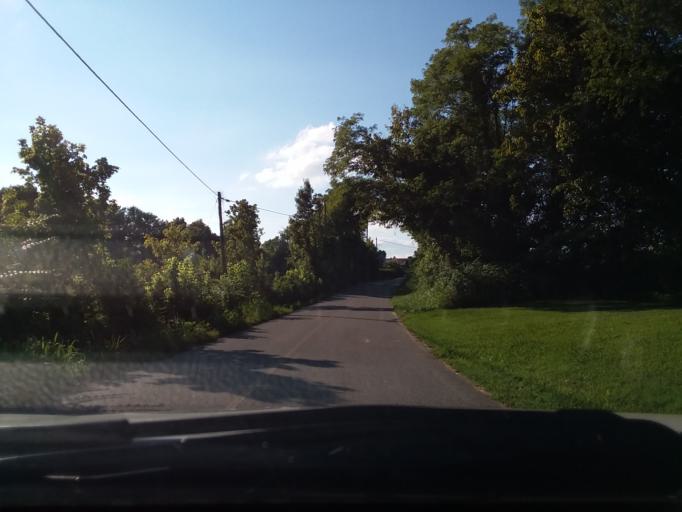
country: US
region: Tennessee
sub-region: Clay County
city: Celina
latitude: 36.6131
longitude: -85.4283
